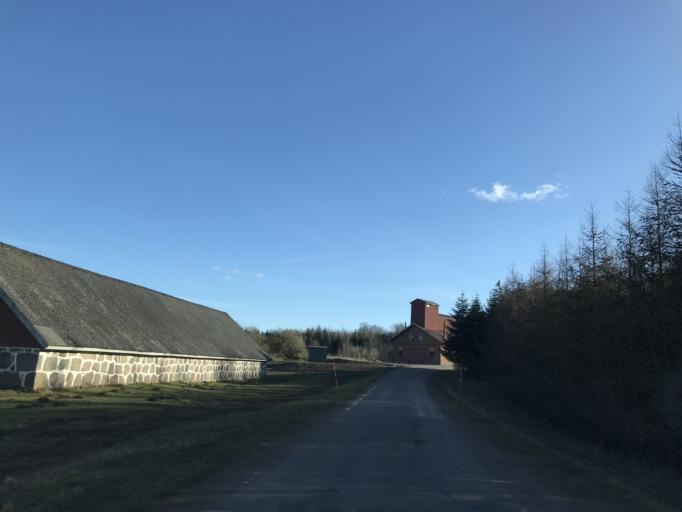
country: SE
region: Skane
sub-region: Ystads Kommun
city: Ystad
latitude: 55.5531
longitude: 13.8076
